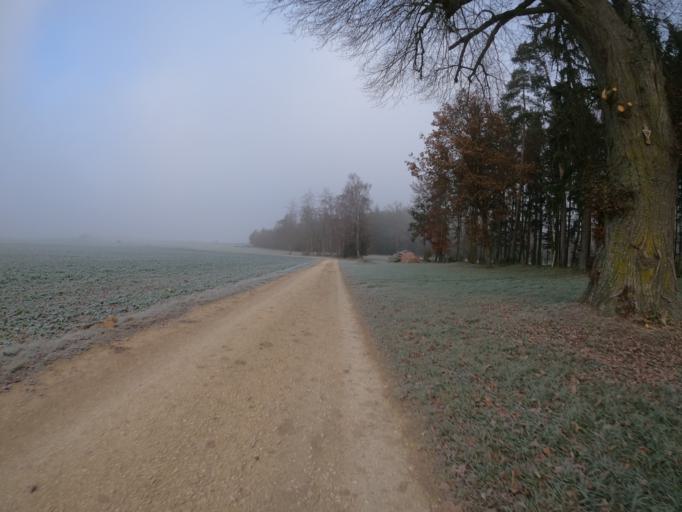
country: DE
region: Baden-Wuerttemberg
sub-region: Tuebingen Region
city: Beimerstetten
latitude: 48.4919
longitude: 9.9663
